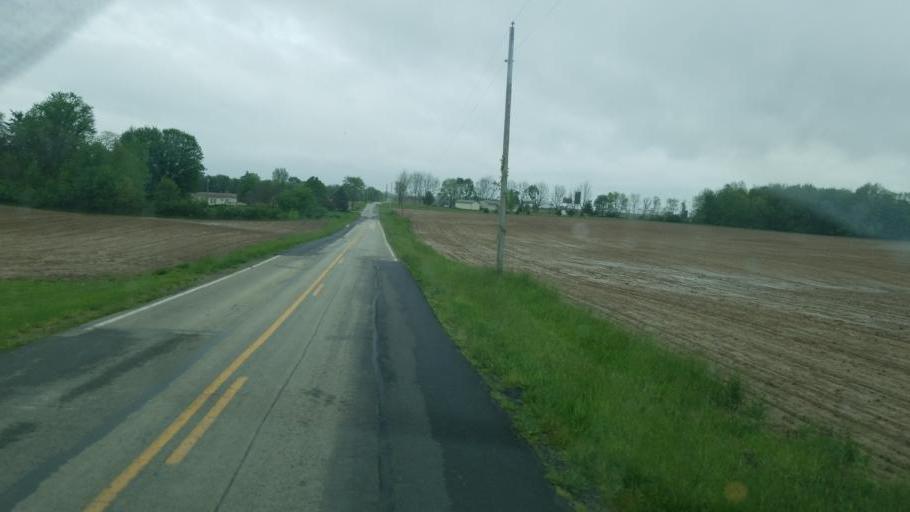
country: US
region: Ohio
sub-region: Highland County
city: Leesburg
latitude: 39.3308
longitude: -83.4974
